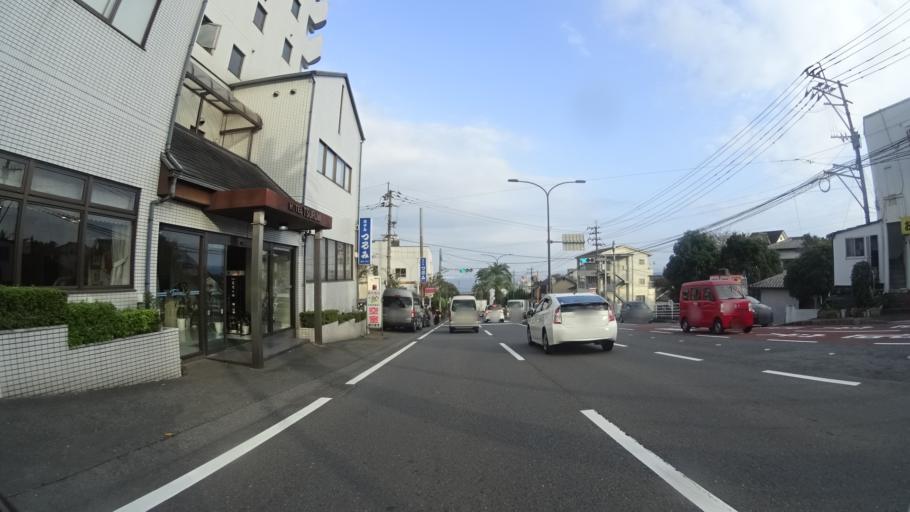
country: JP
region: Oita
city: Beppu
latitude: 33.3138
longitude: 131.4759
